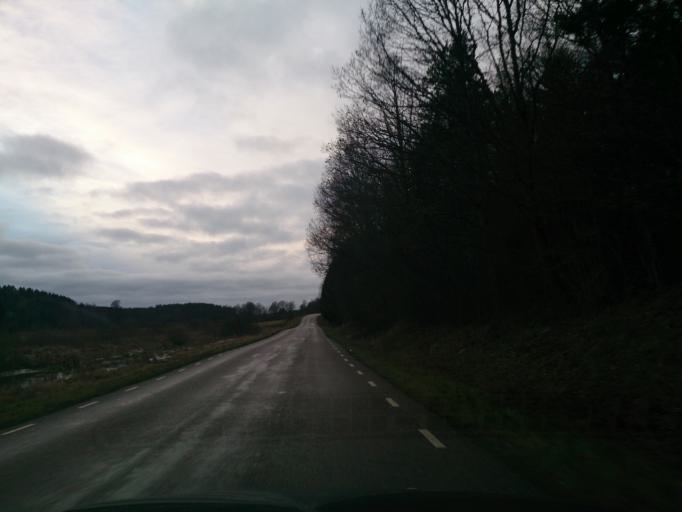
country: SE
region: OEstergoetland
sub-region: Atvidabergs Kommun
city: Atvidaberg
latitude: 58.2893
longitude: 16.0134
